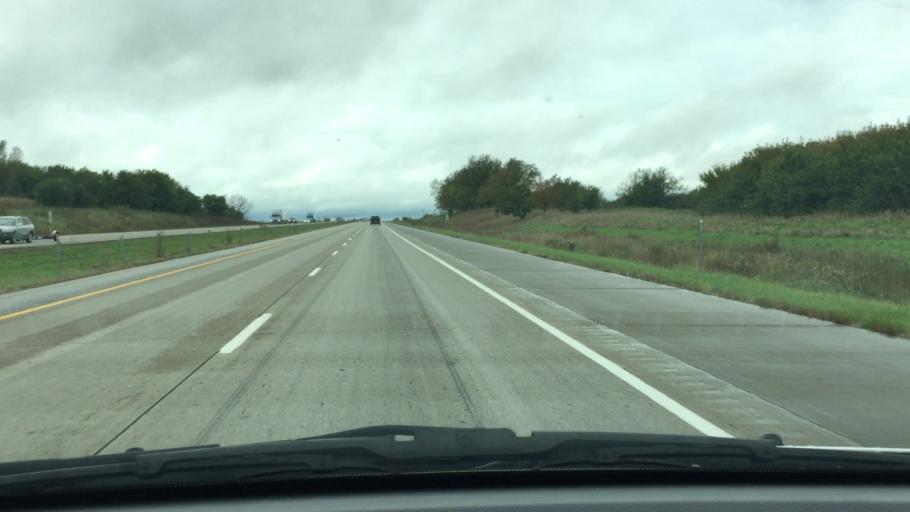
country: US
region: Iowa
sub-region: Polk County
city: Bondurant
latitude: 41.6764
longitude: -93.4218
